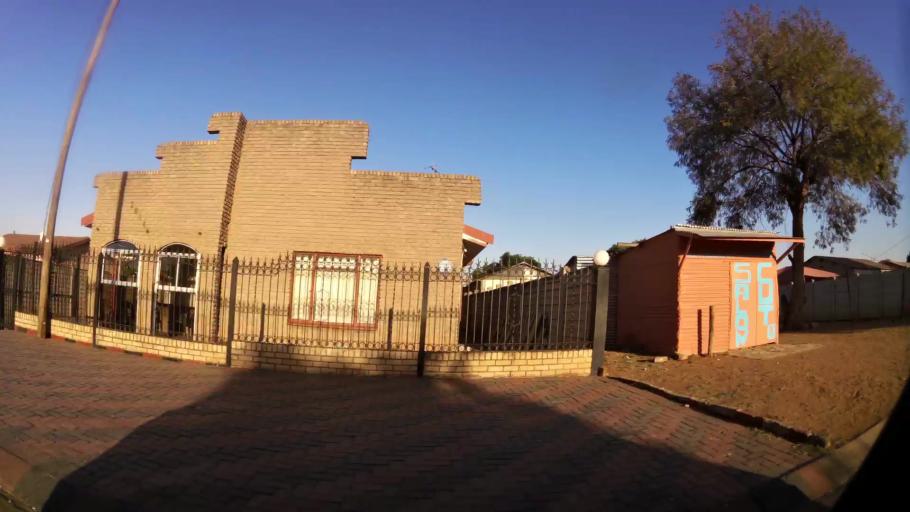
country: ZA
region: North-West
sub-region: Bojanala Platinum District Municipality
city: Rustenburg
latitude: -25.6327
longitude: 27.2095
